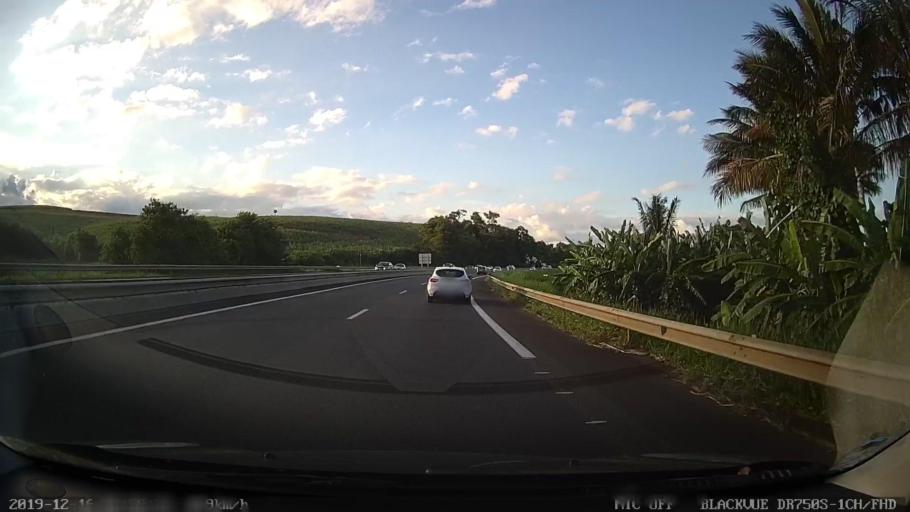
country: RE
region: Reunion
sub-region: Reunion
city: Sainte-Suzanne
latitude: -20.9260
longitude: 55.6293
